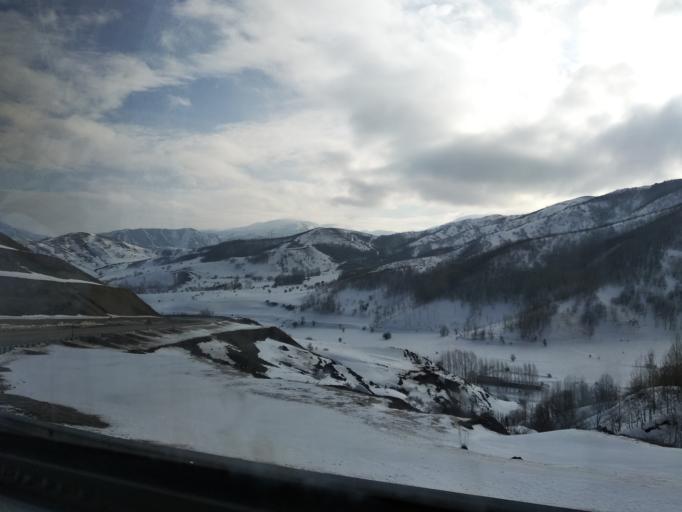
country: TR
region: Erzincan
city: Catalarmut
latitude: 39.8991
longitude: 39.3929
